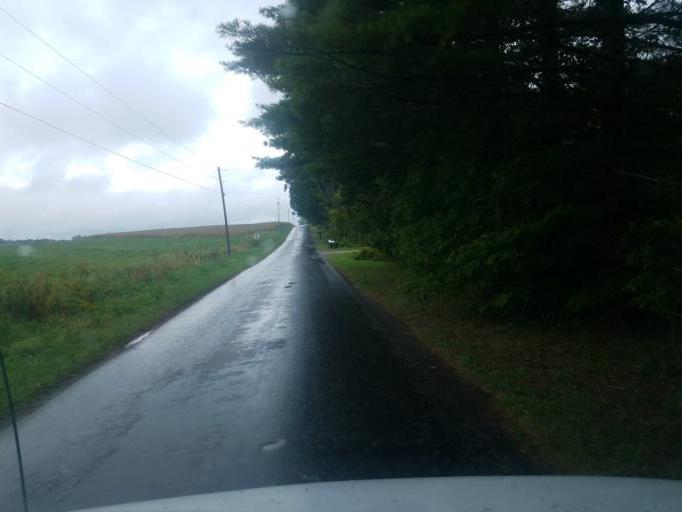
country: US
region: Ohio
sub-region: Wayne County
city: West Salem
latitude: 40.9417
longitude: -82.1328
